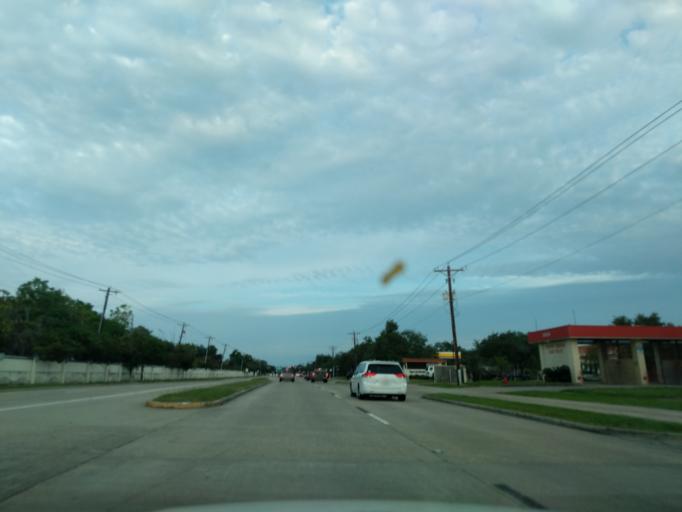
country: US
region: Texas
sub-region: Galveston County
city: Clear Lake Shores
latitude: 29.5258
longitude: -95.0520
